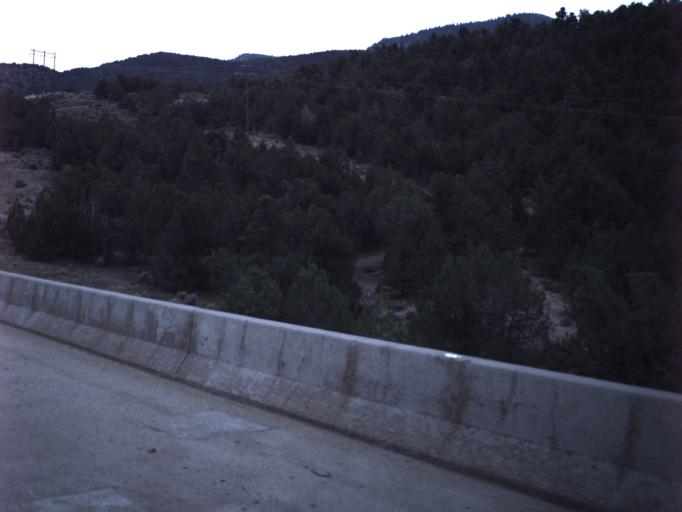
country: US
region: Utah
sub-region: Sevier County
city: Monroe
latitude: 38.5477
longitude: -112.3802
